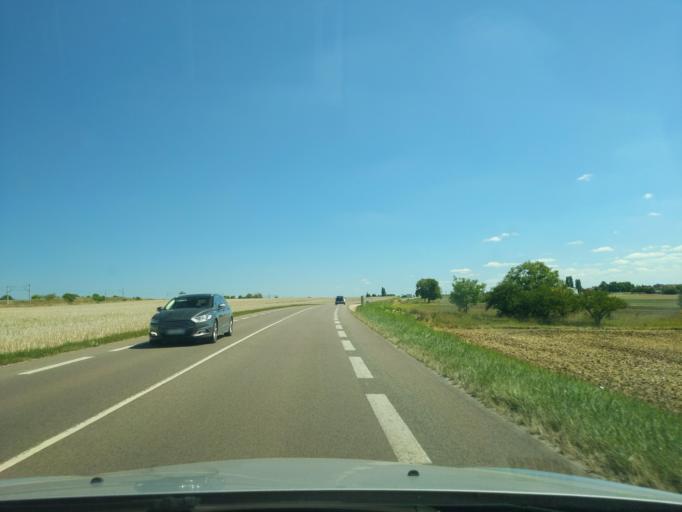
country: FR
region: Bourgogne
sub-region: Departement de la Cote-d'Or
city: Ruffey-les-Echirey
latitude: 47.3623
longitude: 5.0689
